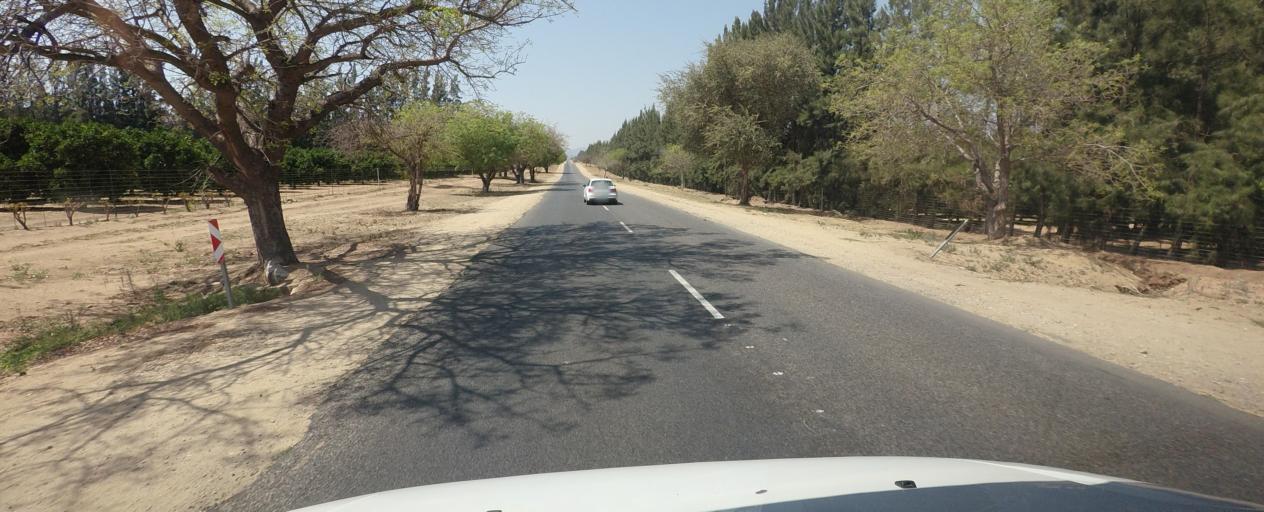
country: ZA
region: Limpopo
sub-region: Mopani District Municipality
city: Hoedspruit
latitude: -24.4355
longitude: 30.8492
